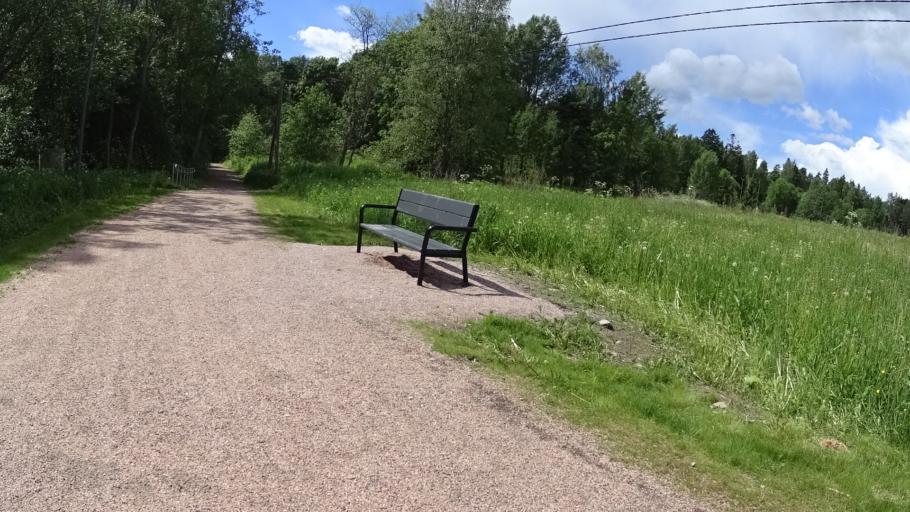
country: FI
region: Uusimaa
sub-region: Helsinki
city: Kauniainen
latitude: 60.2279
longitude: 24.6953
